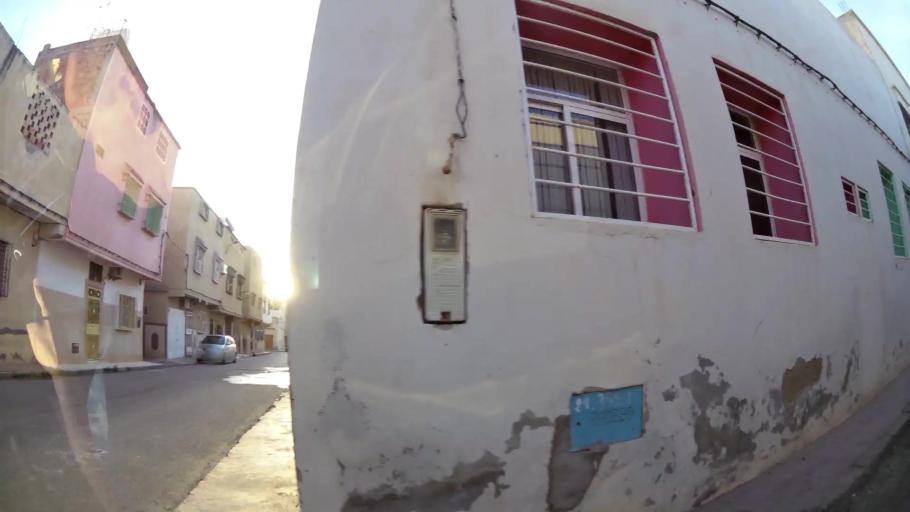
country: MA
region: Oriental
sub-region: Oujda-Angad
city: Oujda
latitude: 34.6780
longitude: -1.8863
